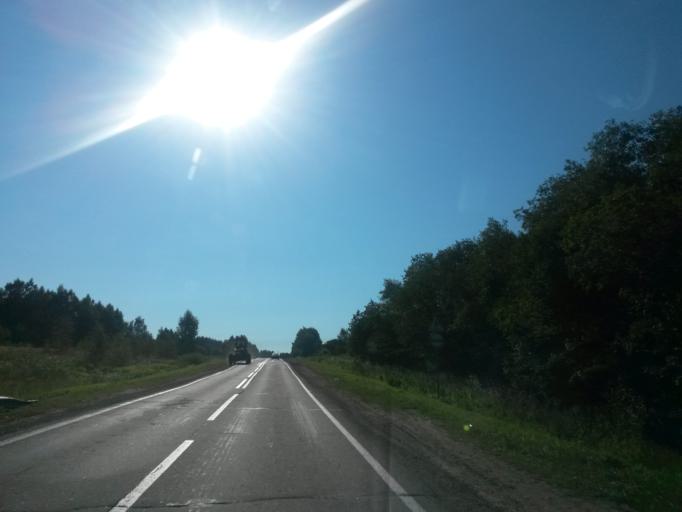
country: RU
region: Jaroslavl
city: Krasnyye Tkachi
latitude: 57.3859
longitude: 39.6978
